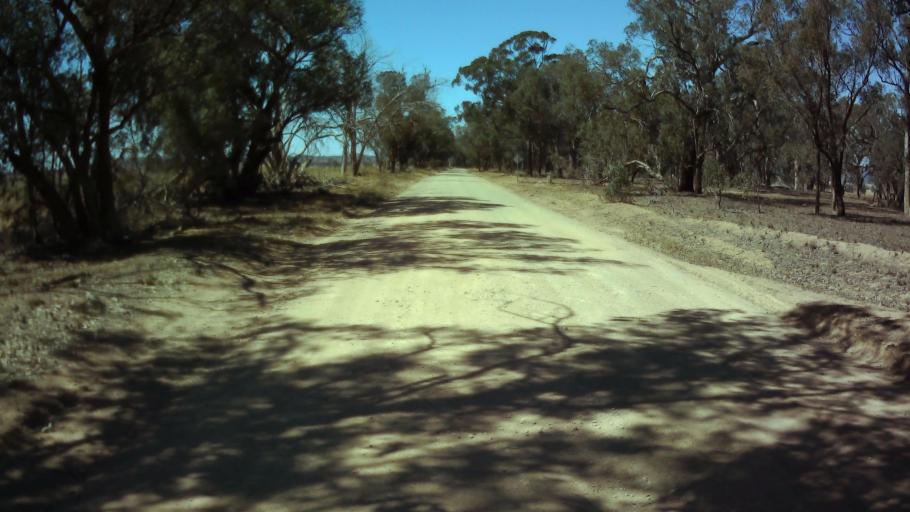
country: AU
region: New South Wales
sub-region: Weddin
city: Grenfell
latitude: -33.8743
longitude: 148.0887
